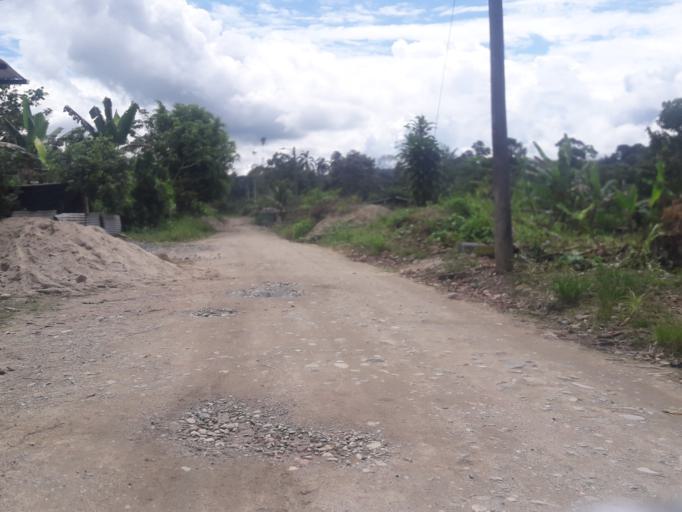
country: EC
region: Napo
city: Tena
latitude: -0.9793
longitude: -77.8518
